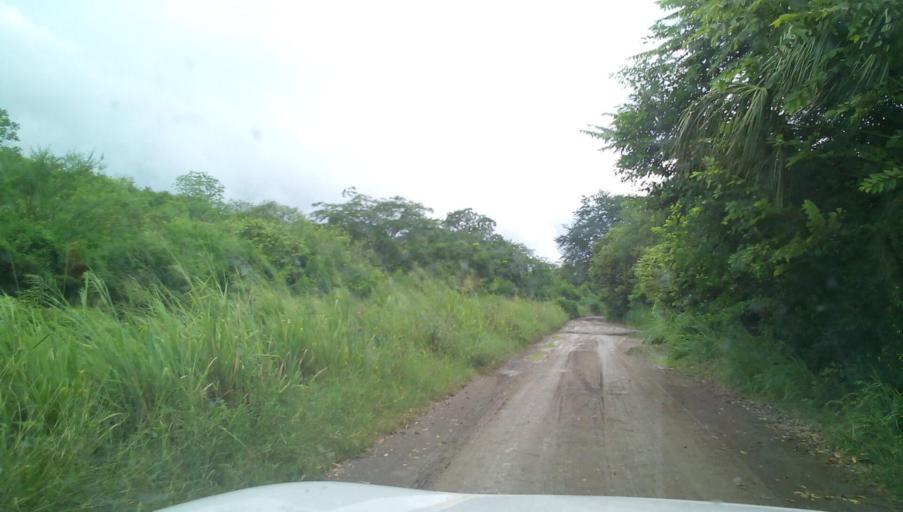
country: MX
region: Veracruz
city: Panuco
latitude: 21.8096
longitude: -98.1089
